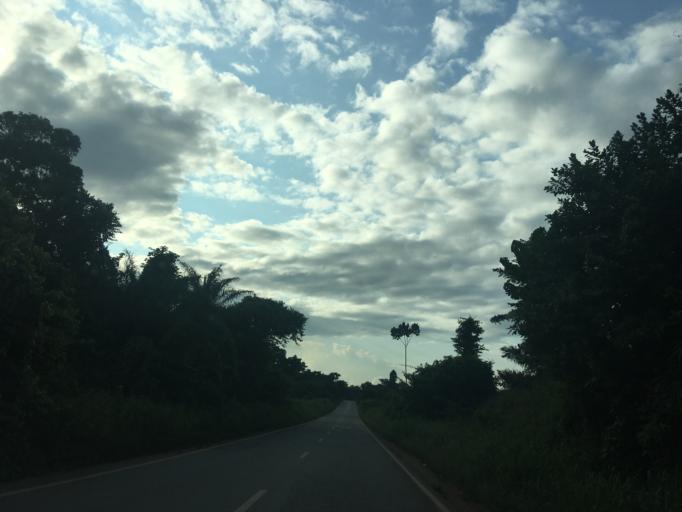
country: GH
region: Western
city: Bibiani
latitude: 6.3444
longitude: -2.2751
